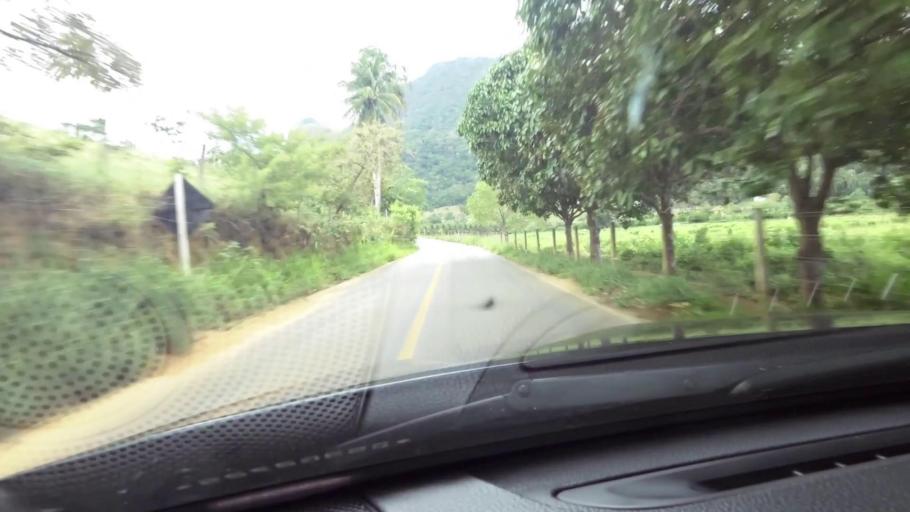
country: BR
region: Espirito Santo
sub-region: Guarapari
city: Guarapari
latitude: -20.6204
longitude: -40.5286
